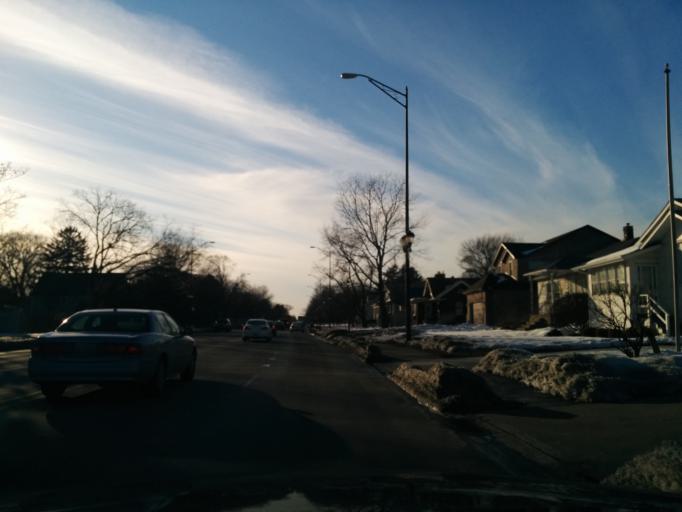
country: US
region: Illinois
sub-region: DuPage County
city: Elmhurst
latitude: 41.9065
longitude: -87.9314
